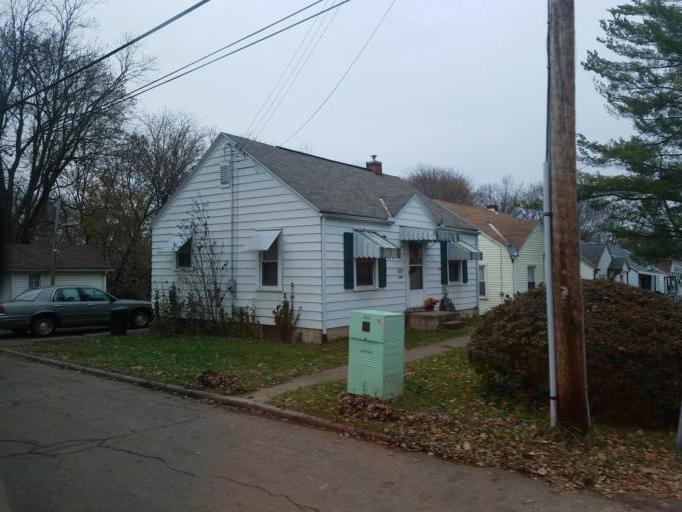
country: US
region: Ohio
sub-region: Richland County
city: Mansfield
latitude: 40.7533
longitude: -82.5077
